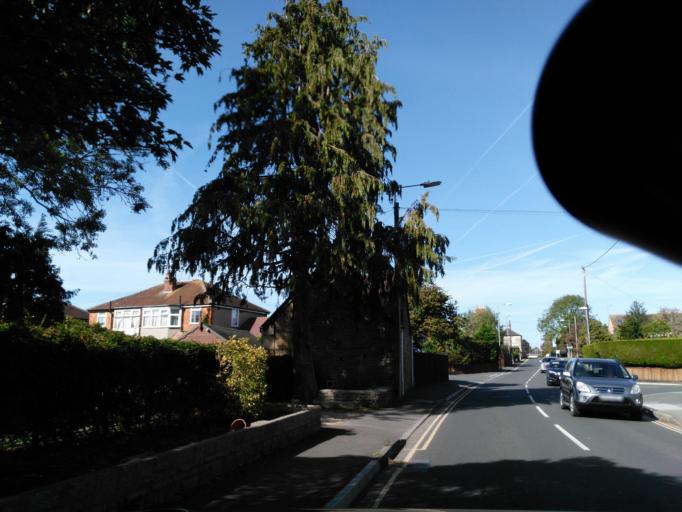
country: GB
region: England
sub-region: Wiltshire
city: Melksham
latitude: 51.3693
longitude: -2.1333
